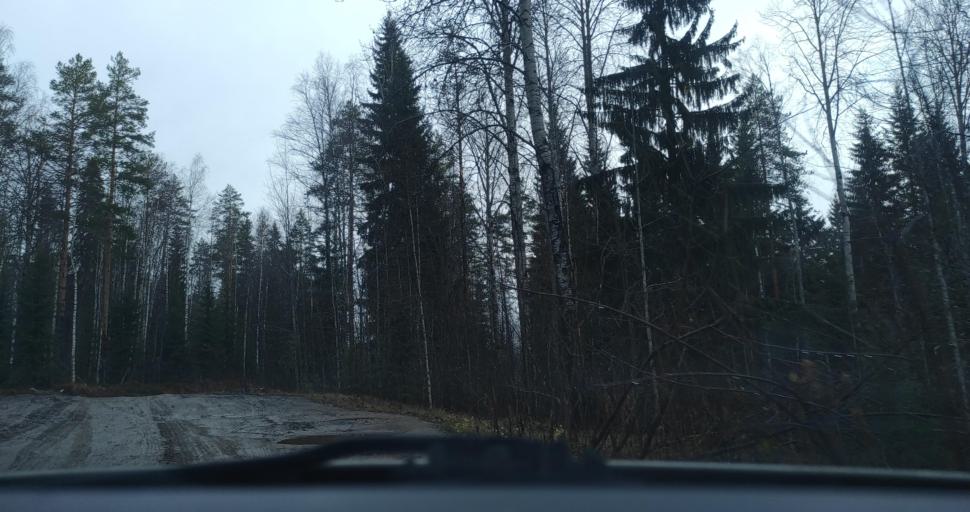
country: RU
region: Republic of Karelia
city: Pitkyaranta
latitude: 61.7448
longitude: 31.3948
